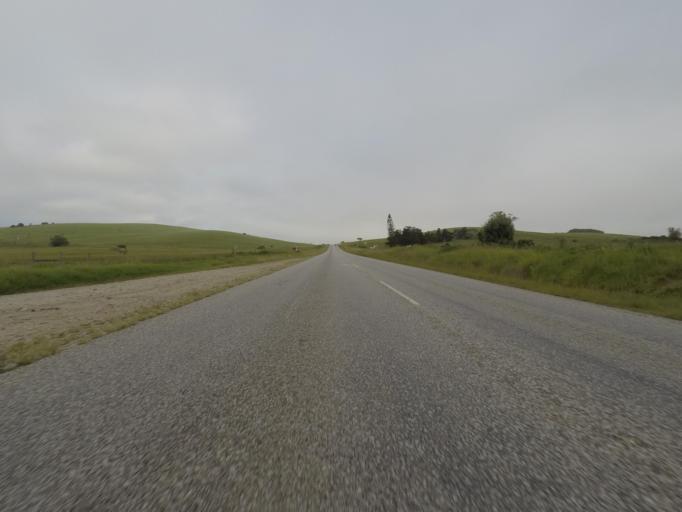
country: ZA
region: Eastern Cape
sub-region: Cacadu District Municipality
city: Port Alfred
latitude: -33.6086
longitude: 26.8148
